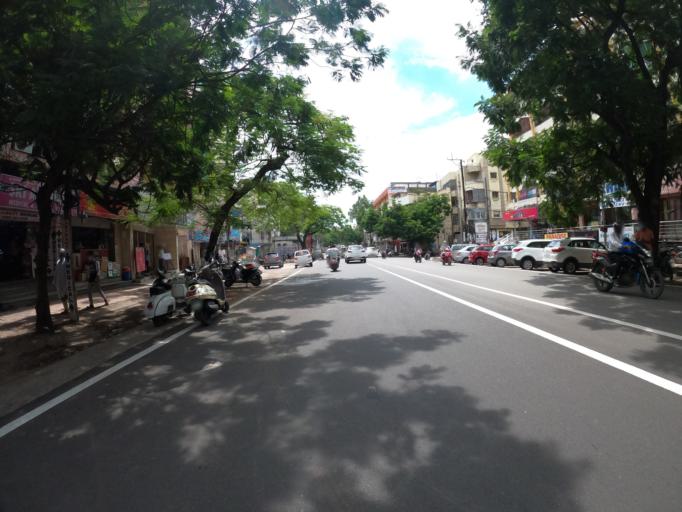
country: IN
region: Telangana
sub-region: Hyderabad
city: Hyderabad
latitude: 17.3989
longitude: 78.4809
